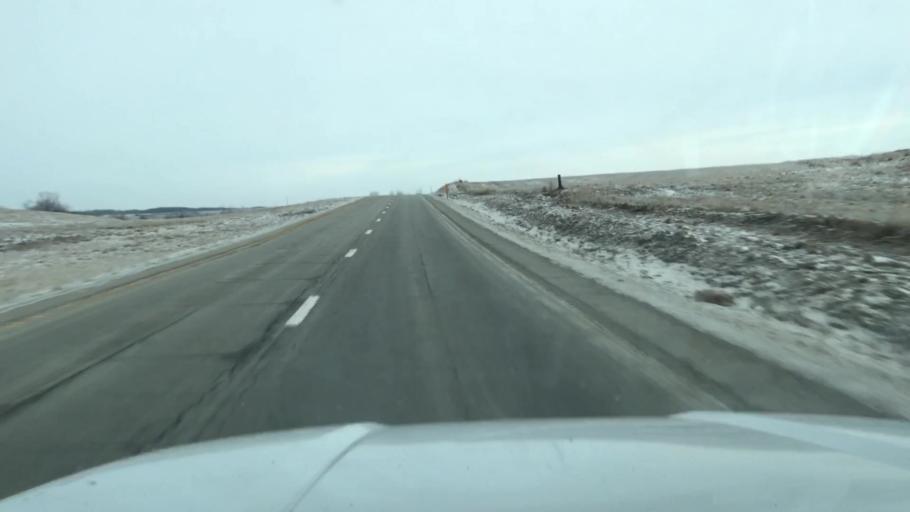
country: US
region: Missouri
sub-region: Andrew County
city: Savannah
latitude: 39.9752
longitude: -94.8756
